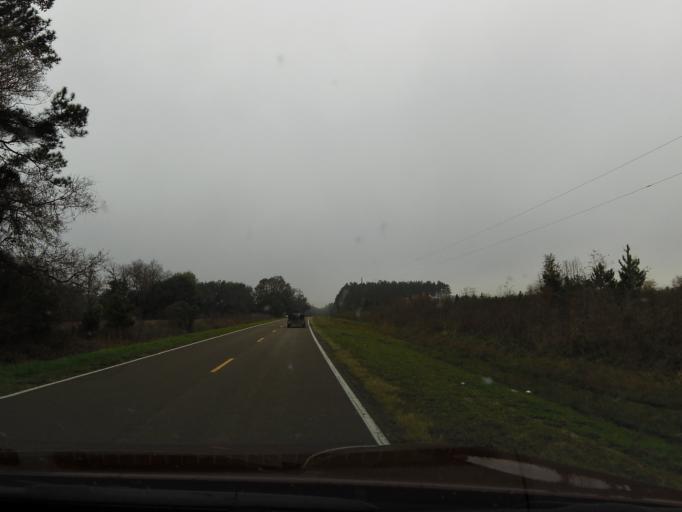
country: US
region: Florida
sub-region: Union County
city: Lake Butler
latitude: 29.9128
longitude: -82.4278
